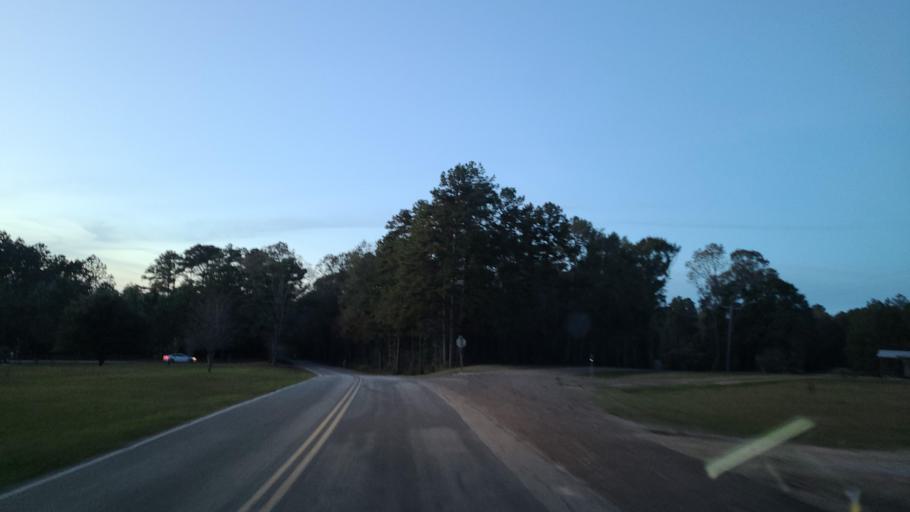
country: US
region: Mississippi
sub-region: Forrest County
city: Hattiesburg
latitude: 31.1777
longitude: -89.2198
